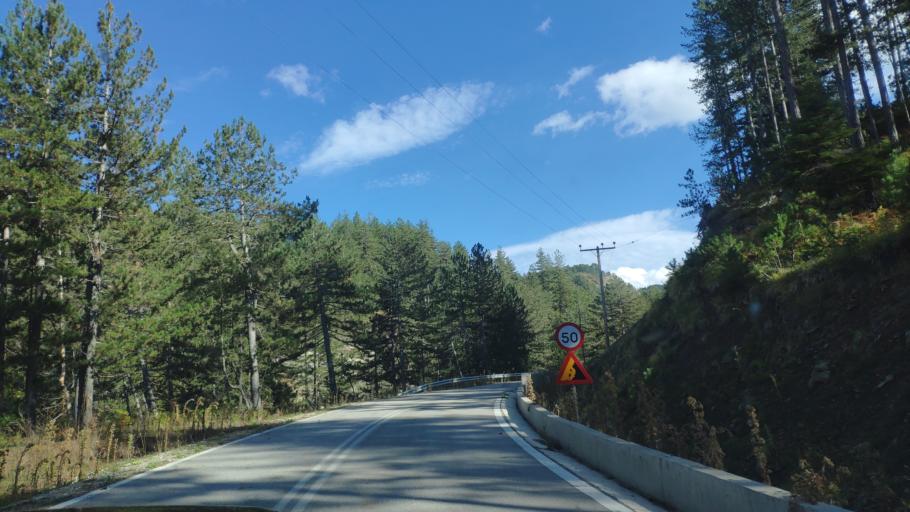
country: AL
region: Korce
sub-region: Rrethi i Devollit
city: Miras
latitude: 40.4051
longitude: 20.8781
